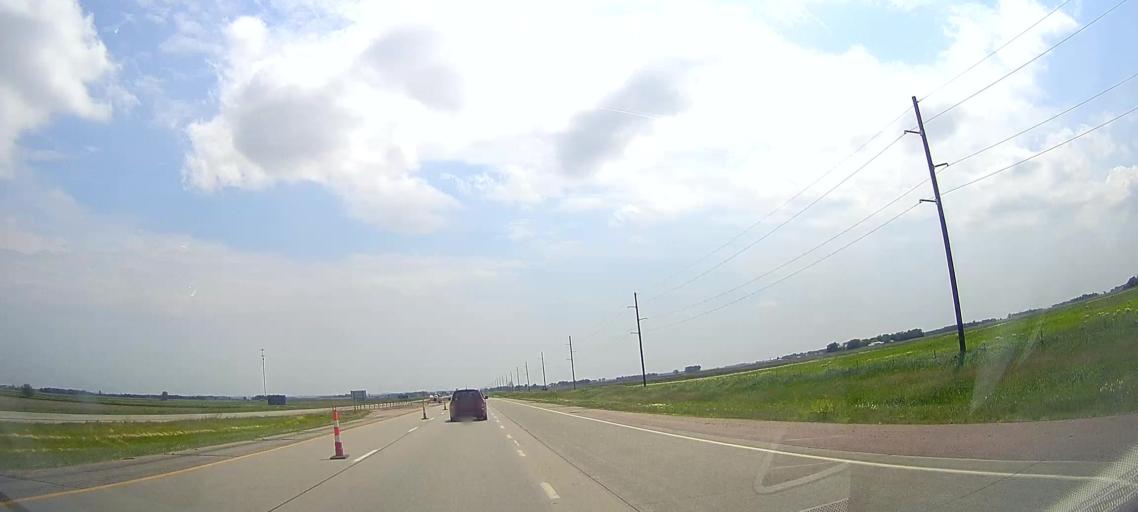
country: US
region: South Dakota
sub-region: Lincoln County
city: Lennox
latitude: 43.2956
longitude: -96.7964
